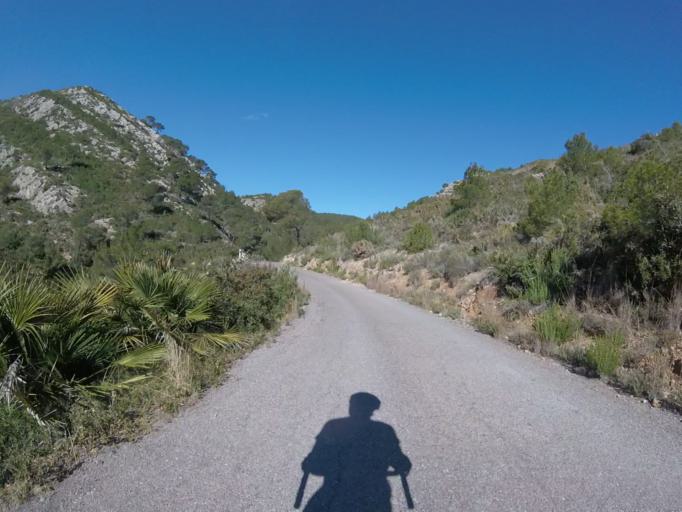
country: ES
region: Valencia
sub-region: Provincia de Castello
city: Benicassim
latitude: 40.0786
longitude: 0.1037
